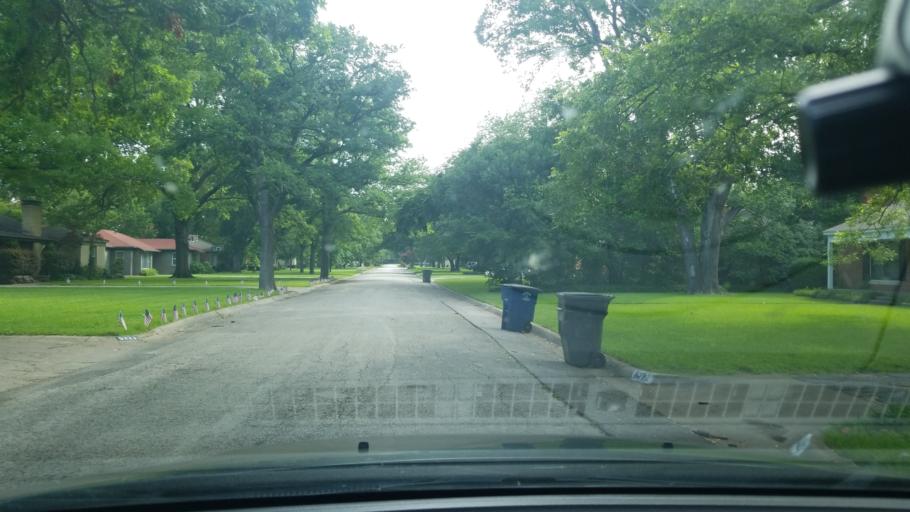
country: US
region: Texas
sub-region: Dallas County
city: Highland Park
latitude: 32.8277
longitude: -96.7045
